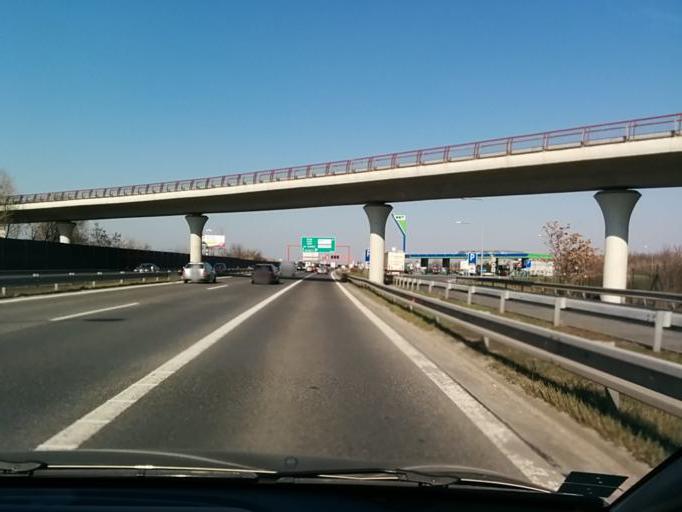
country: SK
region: Bratislavsky
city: Svaty Jur
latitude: 48.1754
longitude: 17.1892
